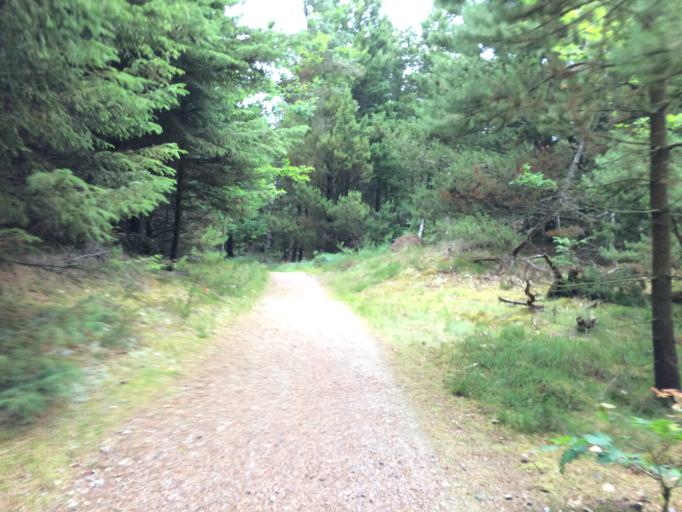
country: DK
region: Central Jutland
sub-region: Holstebro Kommune
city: Ulfborg
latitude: 56.2882
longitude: 8.1499
